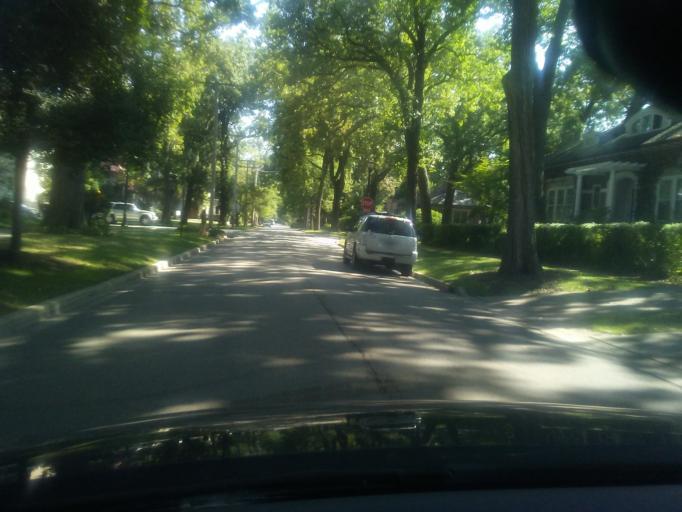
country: US
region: Illinois
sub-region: Cook County
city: Wilmette
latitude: 42.0627
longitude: -87.7034
